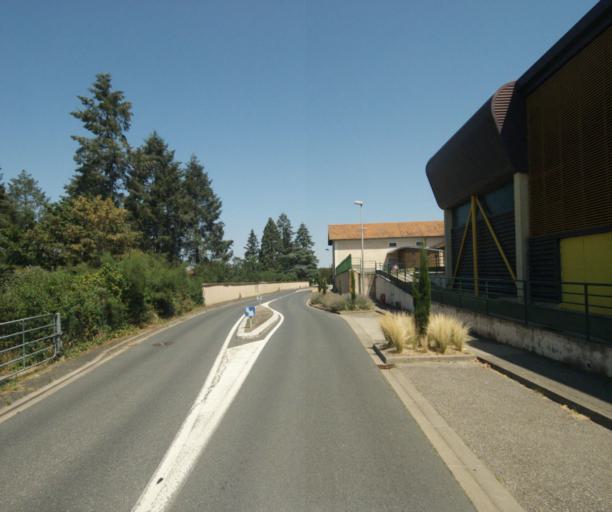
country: FR
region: Rhone-Alpes
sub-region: Departement du Rhone
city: Saint-Pierre-la-Palud
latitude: 45.7948
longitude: 4.6119
